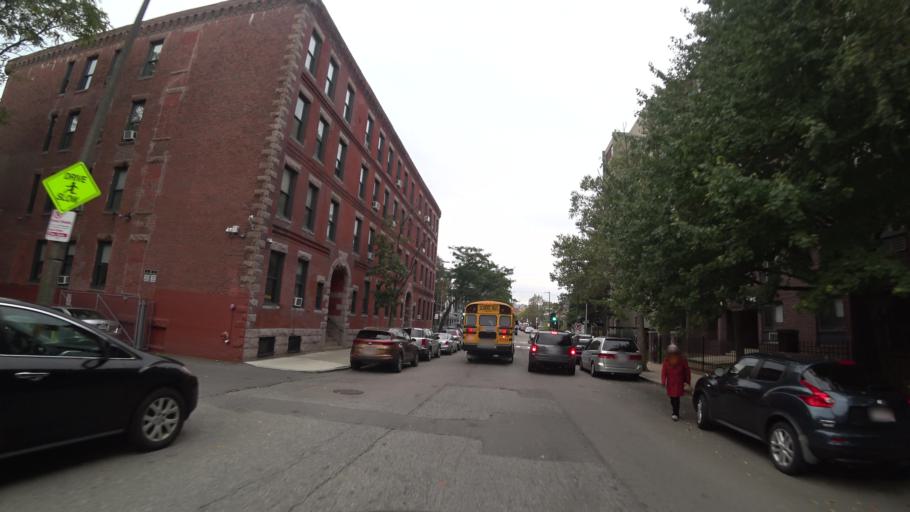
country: US
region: Massachusetts
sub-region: Suffolk County
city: South Boston
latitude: 42.3325
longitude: -71.0837
